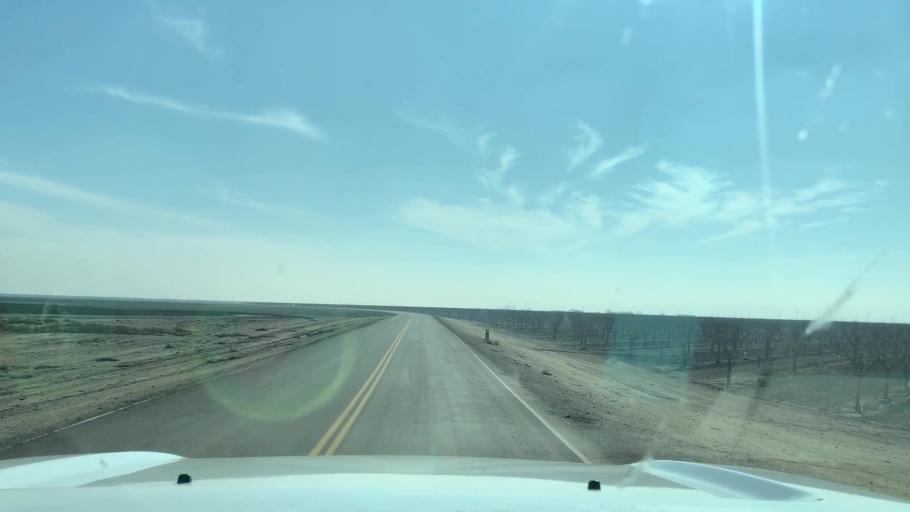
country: US
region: California
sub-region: Kern County
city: Buttonwillow
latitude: 35.4492
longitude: -119.5605
